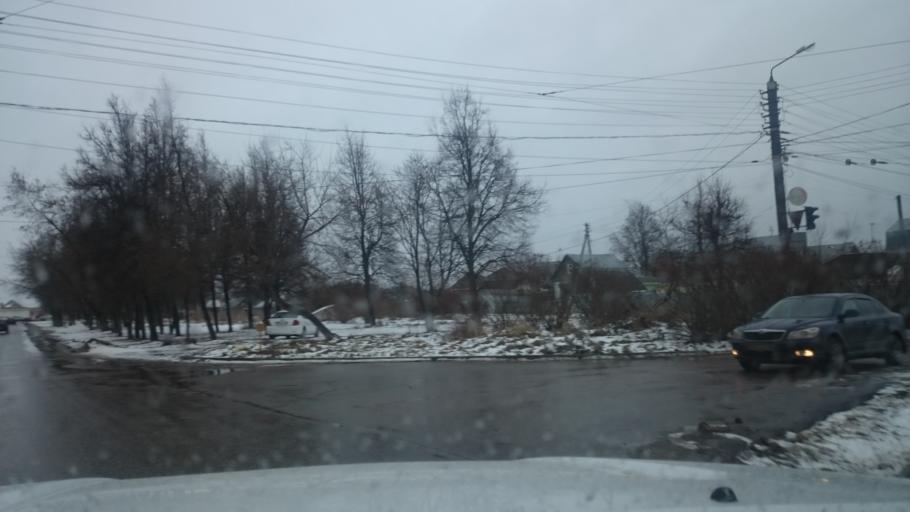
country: RU
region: Tula
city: Mendeleyevskiy
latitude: 54.1955
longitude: 37.5443
